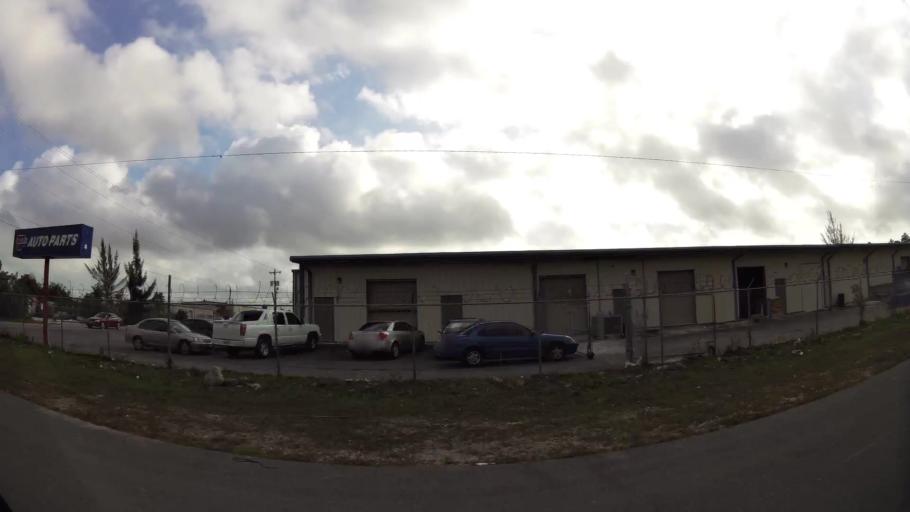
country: BS
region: Freeport
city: Freeport
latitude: 26.5371
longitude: -78.7072
